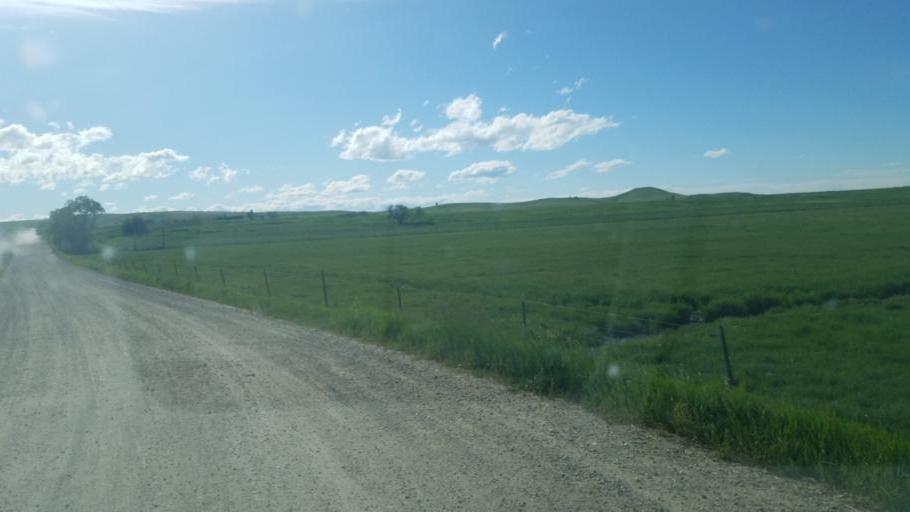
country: US
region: Montana
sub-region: Carbon County
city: Red Lodge
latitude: 45.3636
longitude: -109.1683
